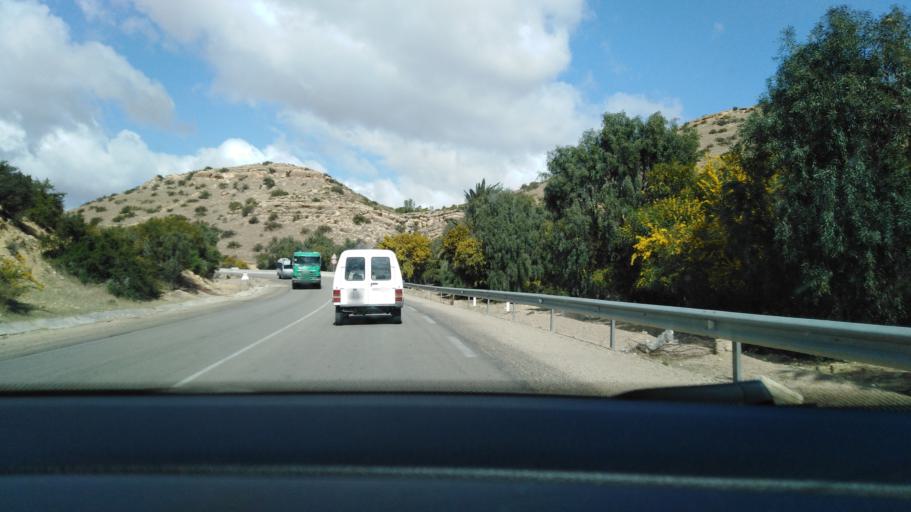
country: TN
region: Al Qayrawan
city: Haffouz
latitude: 35.6339
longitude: 9.8218
